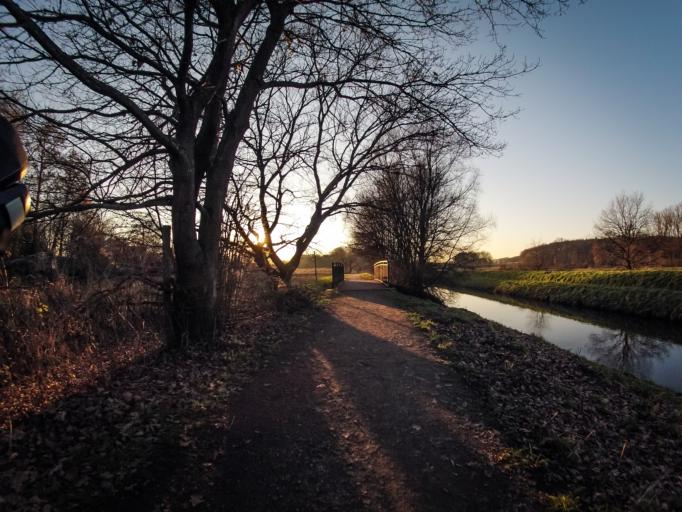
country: DE
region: Lower Saxony
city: Wallenhorst
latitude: 52.3102
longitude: 7.9928
